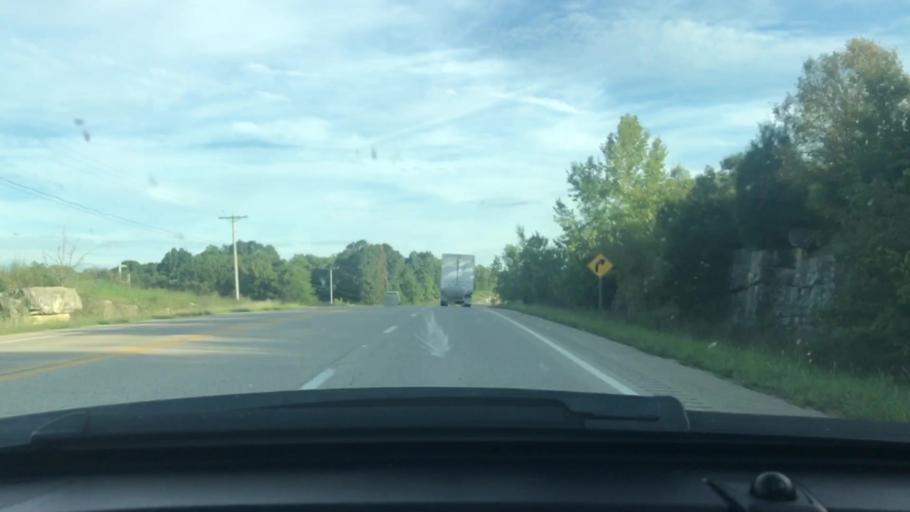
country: US
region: Arkansas
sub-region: Randolph County
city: Pocahontas
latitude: 36.1898
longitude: -91.1641
